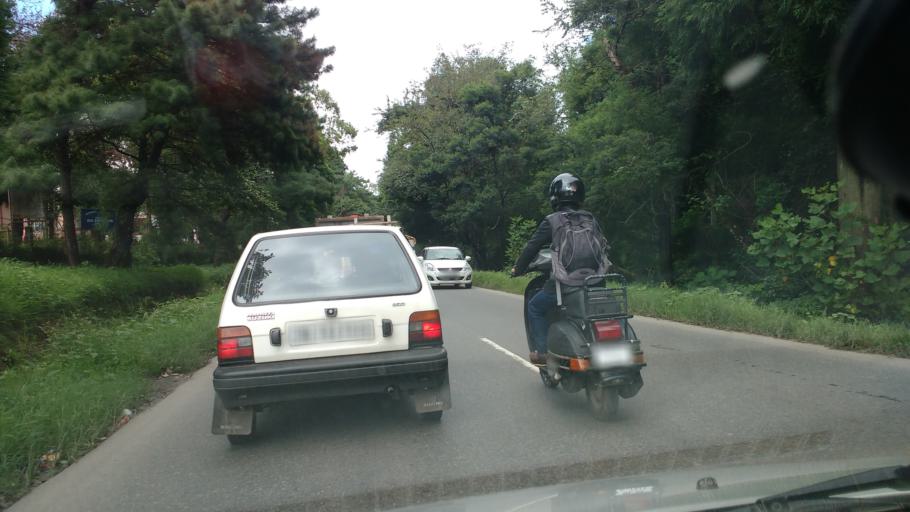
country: IN
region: Meghalaya
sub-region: East Khasi Hills
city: Shillong
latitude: 25.5520
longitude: 91.8437
